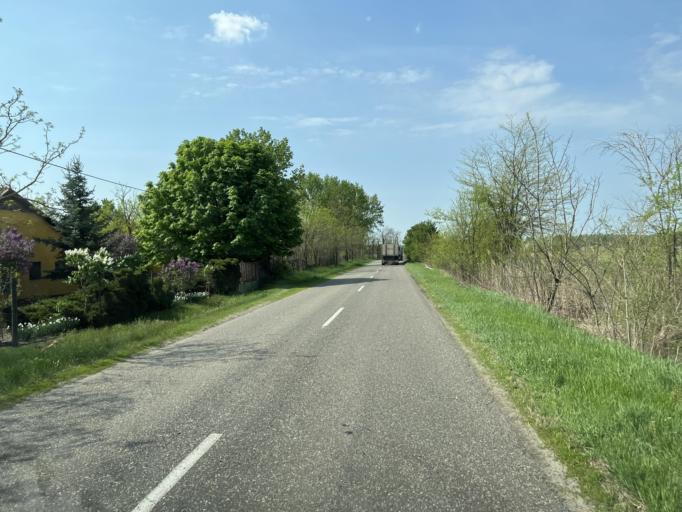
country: HU
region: Pest
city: Tortel
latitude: 47.0953
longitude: 19.8952
